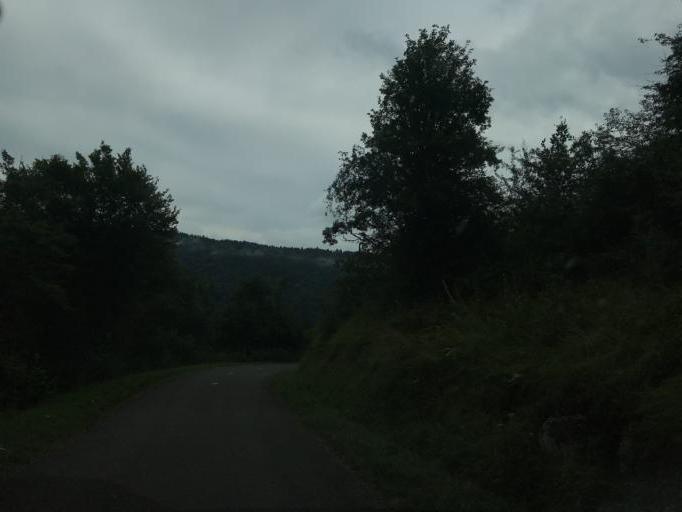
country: FR
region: Franche-Comte
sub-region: Departement du Jura
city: Lavans-les-Saint-Claude
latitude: 46.3225
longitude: 5.7535
